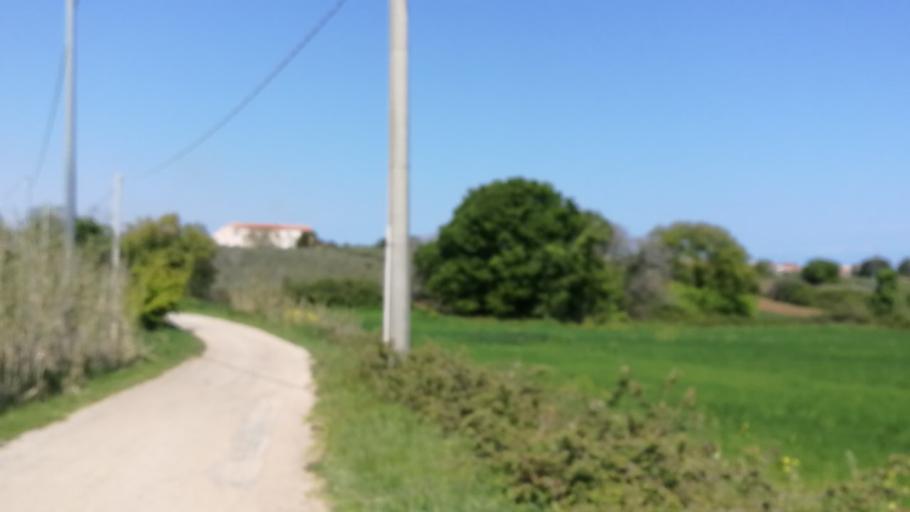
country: IT
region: Molise
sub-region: Provincia di Campobasso
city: Termoli
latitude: 41.9711
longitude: 14.9879
